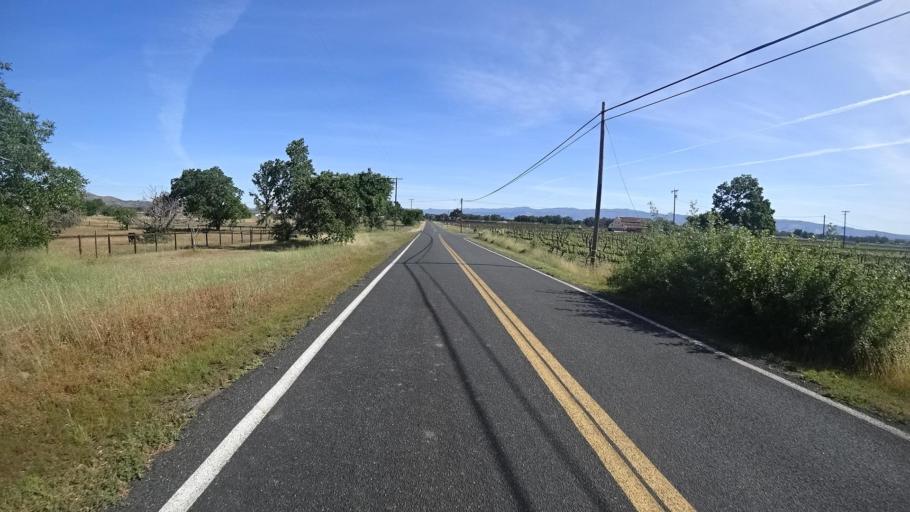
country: US
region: California
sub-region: Lake County
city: Kelseyville
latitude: 38.9823
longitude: -122.8943
